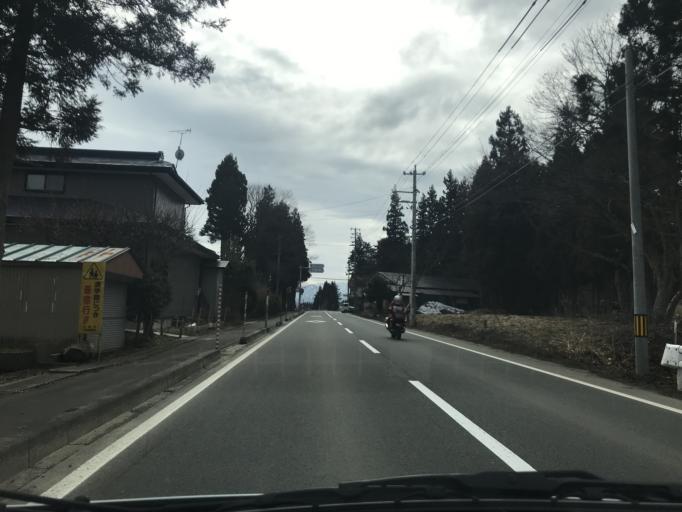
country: JP
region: Iwate
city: Hanamaki
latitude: 39.3550
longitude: 140.9879
